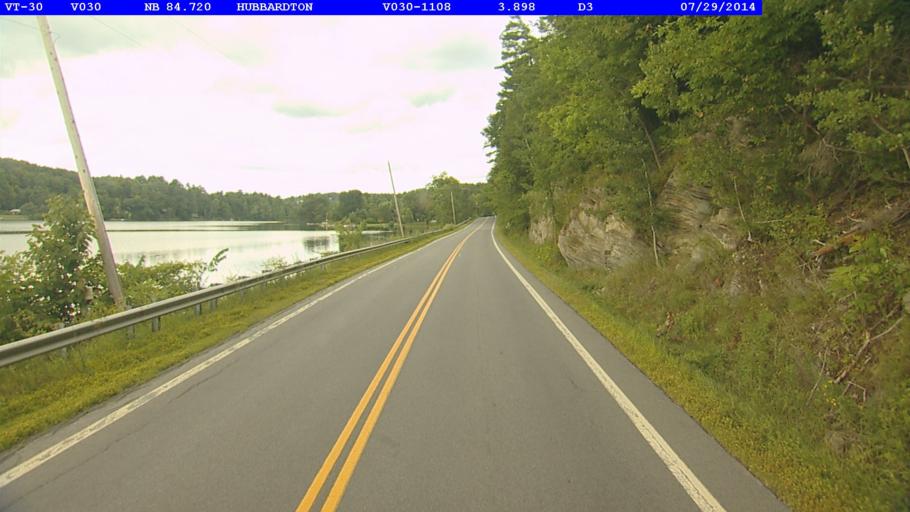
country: US
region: Vermont
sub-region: Rutland County
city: Brandon
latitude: 43.7336
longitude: -73.1802
